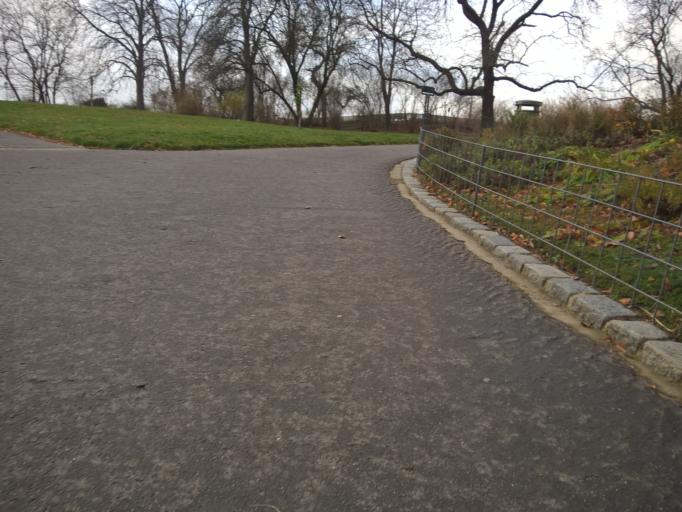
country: CZ
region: Praha
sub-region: Praha 2
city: Vysehrad
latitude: 50.0632
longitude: 14.4210
